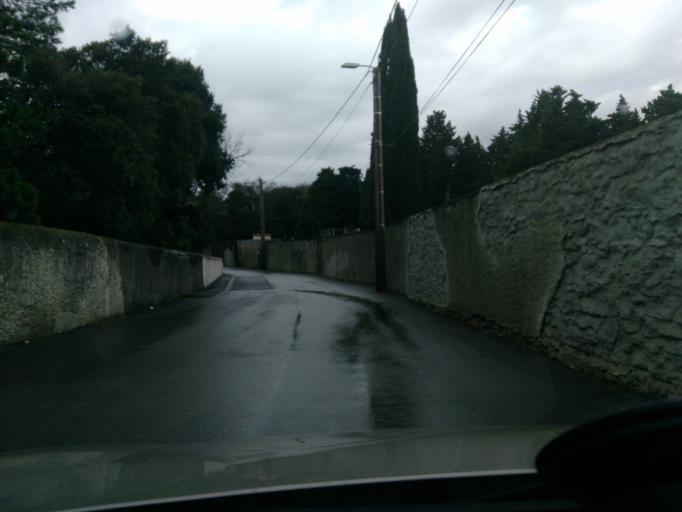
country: FR
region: Rhone-Alpes
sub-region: Departement de la Drome
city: Montelimar
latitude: 44.5631
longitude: 4.7582
